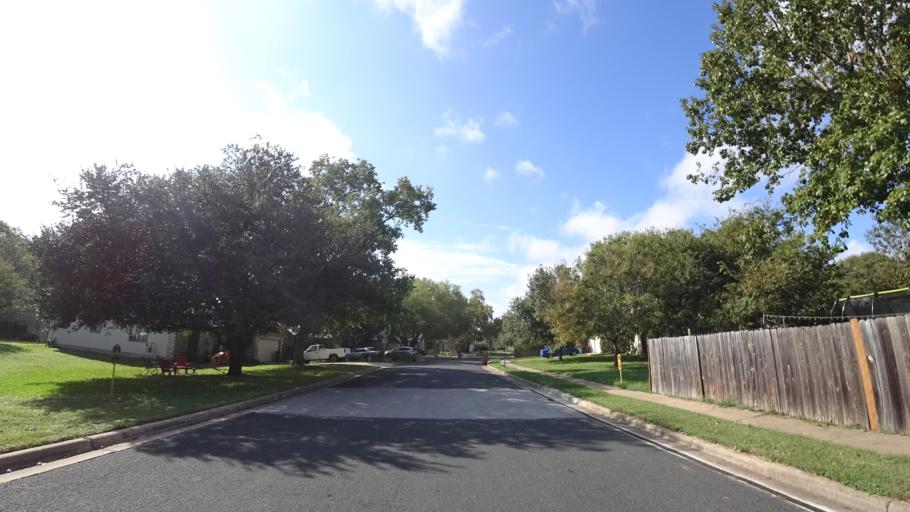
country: US
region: Texas
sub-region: Travis County
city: Shady Hollow
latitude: 30.1941
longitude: -97.8248
